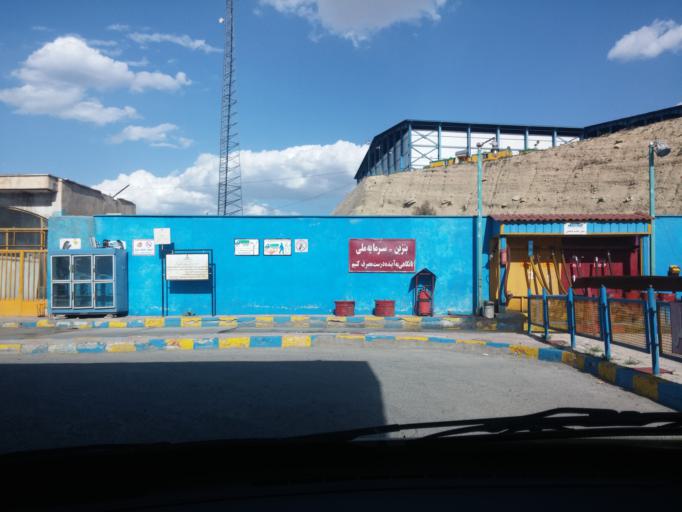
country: IR
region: Tehran
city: Damavand
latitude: 35.7072
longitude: 51.9773
